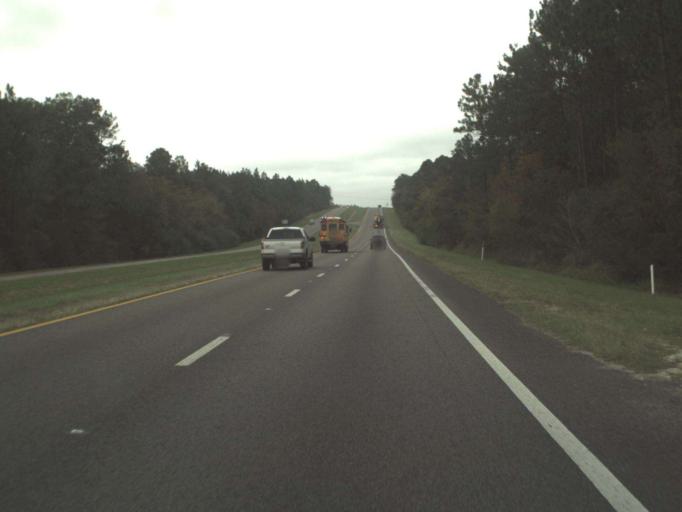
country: US
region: Florida
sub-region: Escambia County
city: Molino
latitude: 30.6883
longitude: -87.3507
